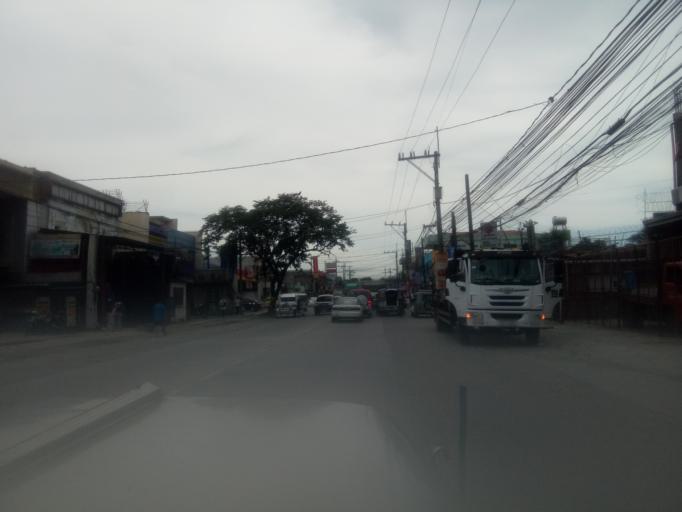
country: PH
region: Calabarzon
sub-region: Province of Cavite
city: Bulihan
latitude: 14.2854
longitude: 121.0002
